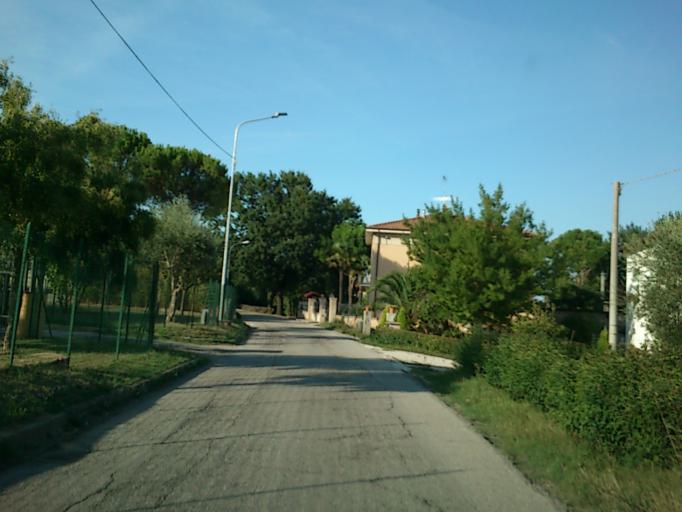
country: IT
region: The Marches
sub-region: Provincia di Pesaro e Urbino
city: Saltara
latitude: 43.7407
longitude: 12.9090
